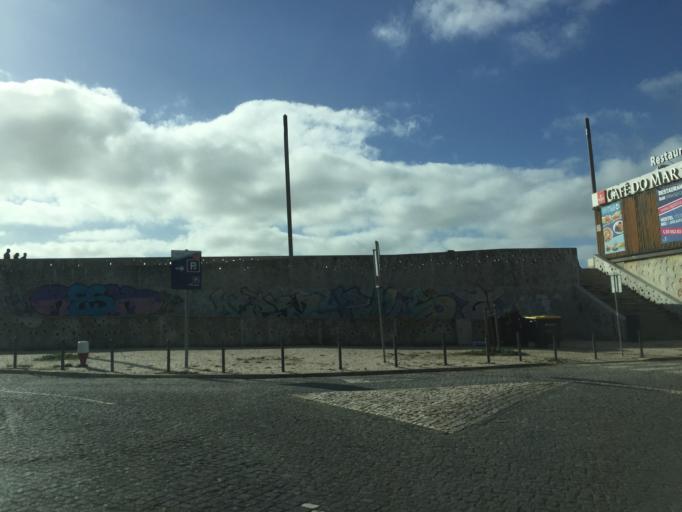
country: PT
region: Setubal
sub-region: Almada
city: Costa de Caparica
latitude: 38.6465
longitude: -9.2420
